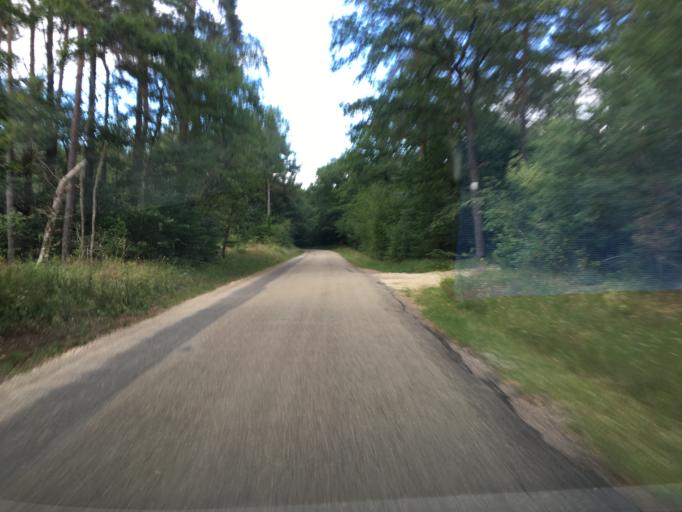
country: FR
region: Bourgogne
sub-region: Departement de l'Yonne
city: Charbuy
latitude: 47.8562
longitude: 3.4870
